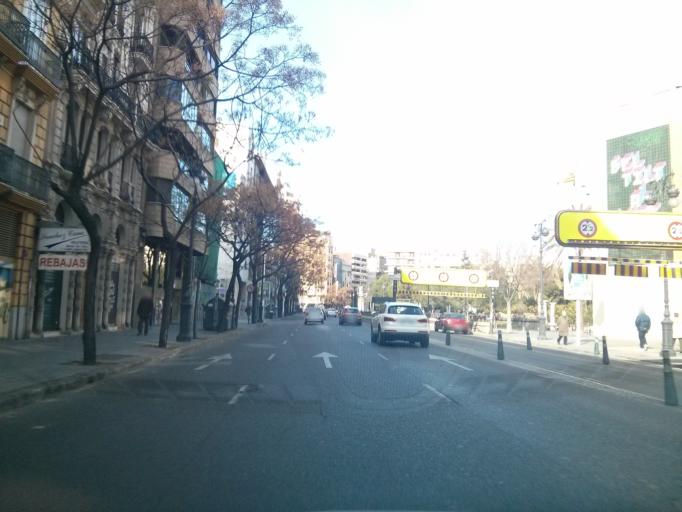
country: ES
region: Valencia
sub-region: Provincia de Valencia
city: Valencia
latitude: 39.4690
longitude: -0.3815
